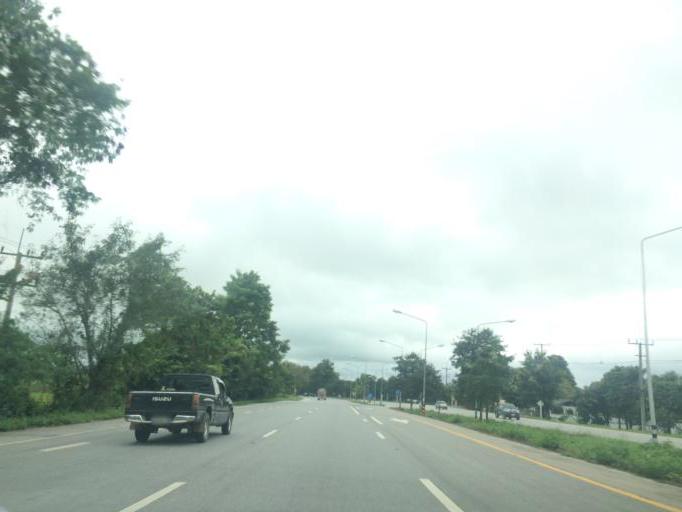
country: TH
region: Chiang Rai
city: Mae Lao
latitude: 19.7981
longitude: 99.7520
